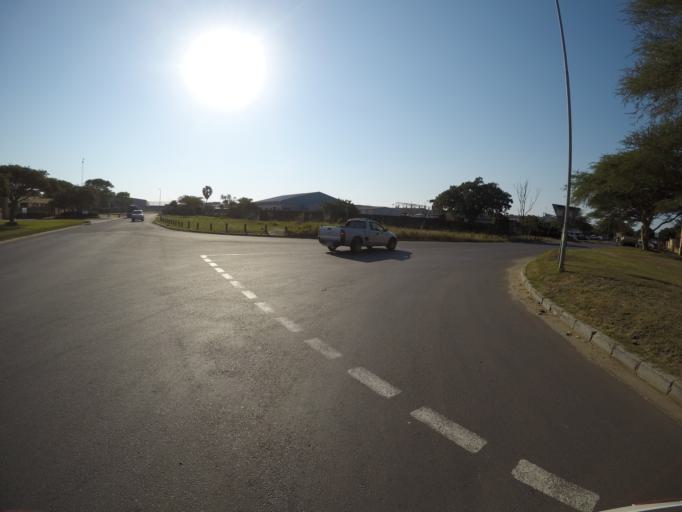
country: ZA
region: KwaZulu-Natal
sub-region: uThungulu District Municipality
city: Richards Bay
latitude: -28.7504
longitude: 32.0215
